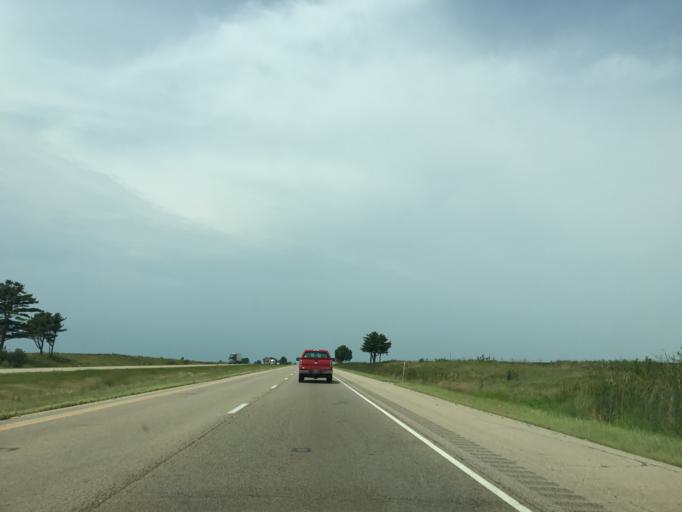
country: US
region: Illinois
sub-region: Bureau County
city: Ladd
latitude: 41.3885
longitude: -89.2801
